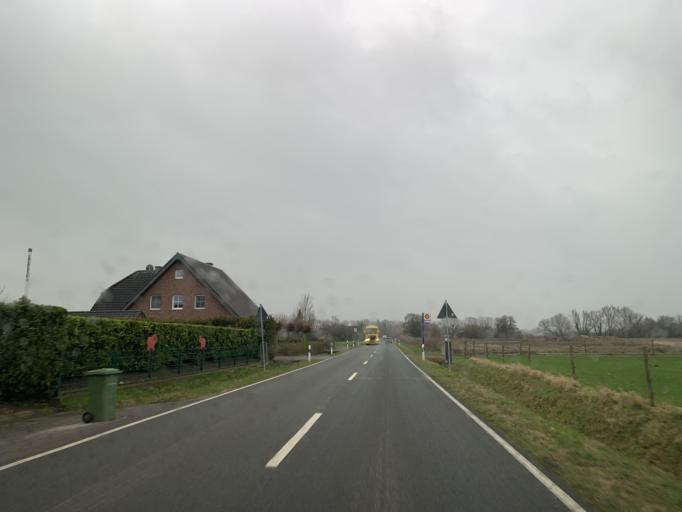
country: DE
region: North Rhine-Westphalia
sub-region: Regierungsbezirk Munster
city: Dulmen
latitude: 51.8536
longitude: 7.3492
